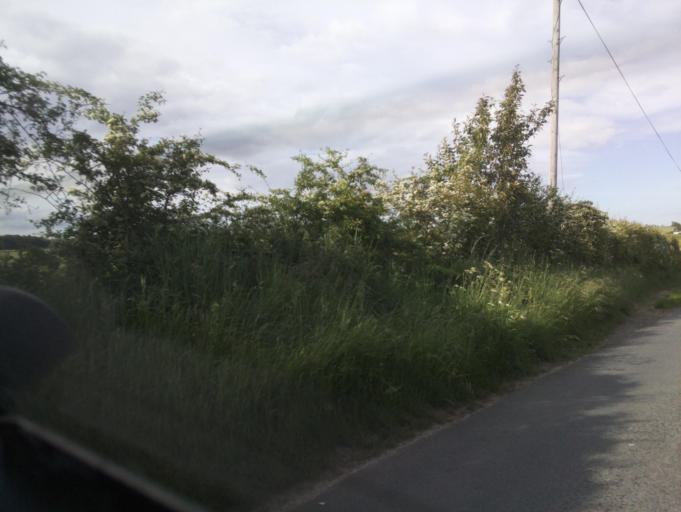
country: GB
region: England
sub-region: Gloucestershire
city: Donnington
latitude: 51.9552
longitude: -1.7742
